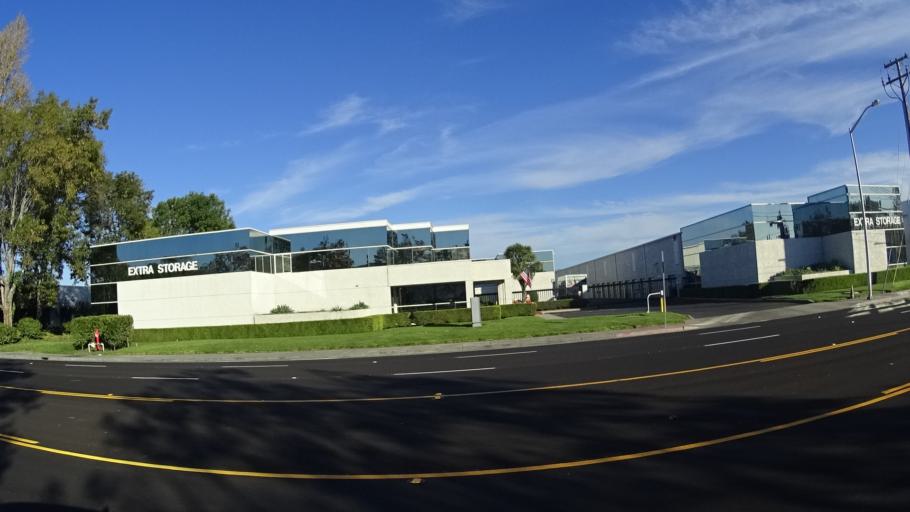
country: US
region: California
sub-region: Santa Clara County
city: Santa Clara
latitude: 37.3712
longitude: -121.9597
